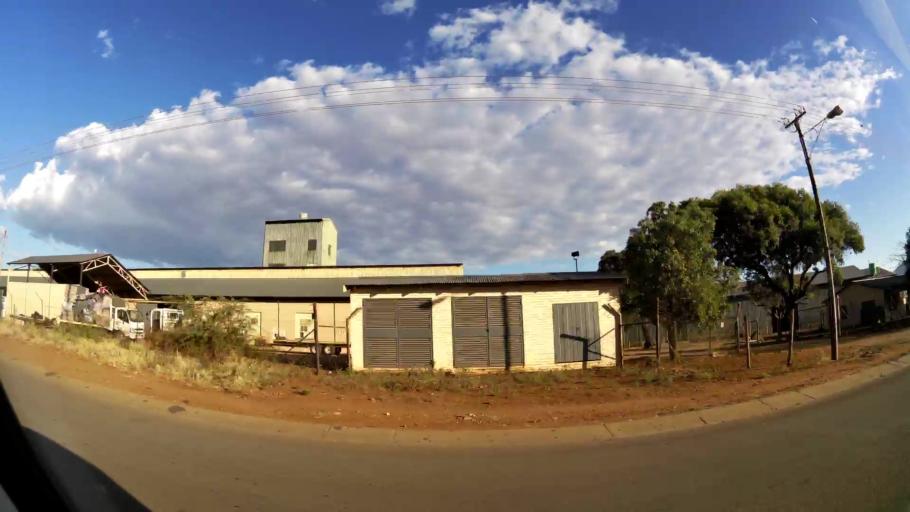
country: ZA
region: Limpopo
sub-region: Waterberg District Municipality
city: Mokopane
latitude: -24.1707
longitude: 29.0008
